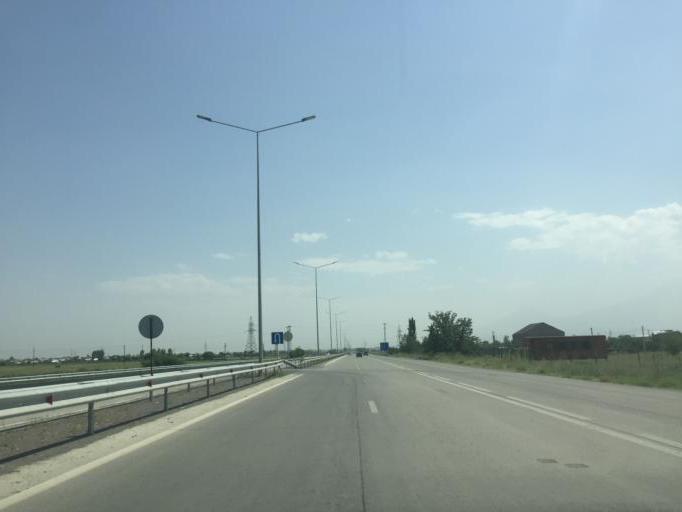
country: AM
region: Ararat
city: Masis
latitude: 40.0738
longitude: 44.4548
